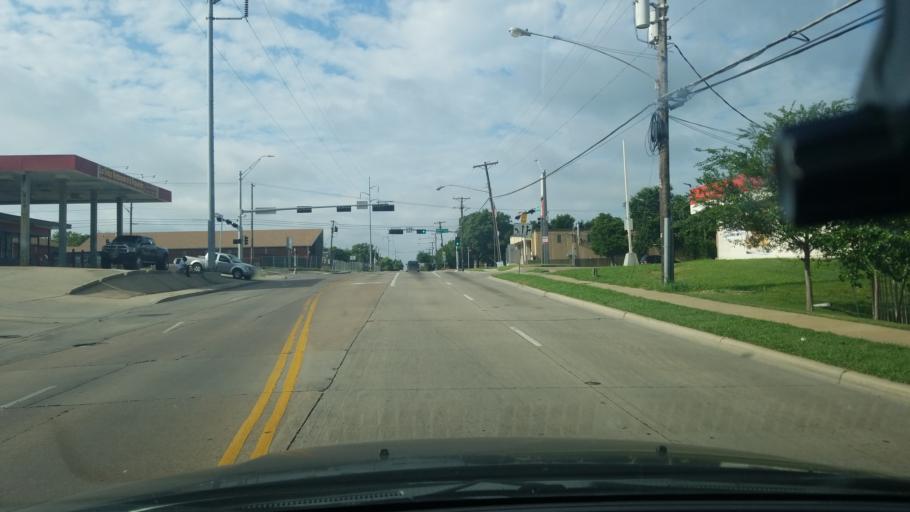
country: US
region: Texas
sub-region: Dallas County
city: Balch Springs
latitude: 32.7495
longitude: -96.6569
